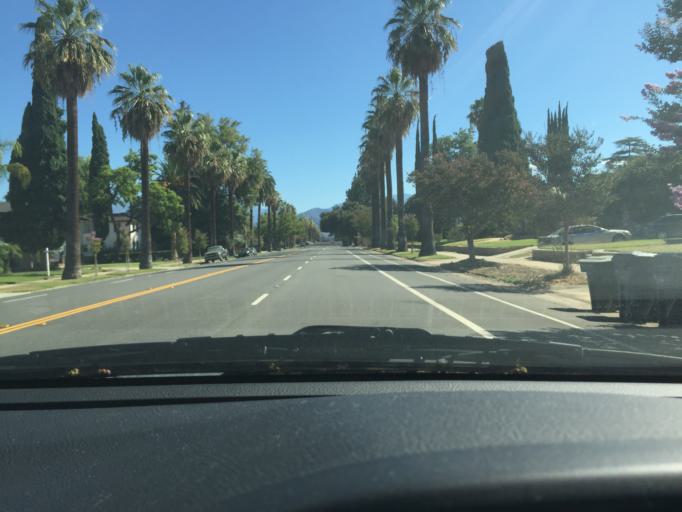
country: US
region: California
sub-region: San Bernardino County
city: Redlands
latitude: 34.0454
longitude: -117.1800
